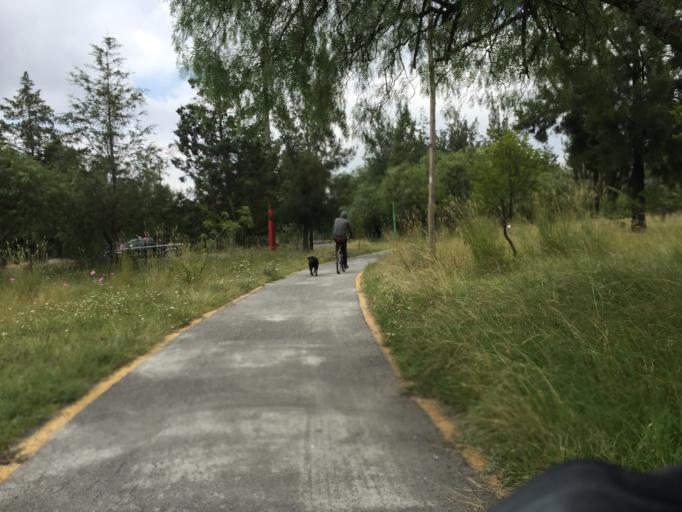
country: MX
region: Mexico
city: Cuautitlan Izcalli
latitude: 19.6540
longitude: -99.2016
